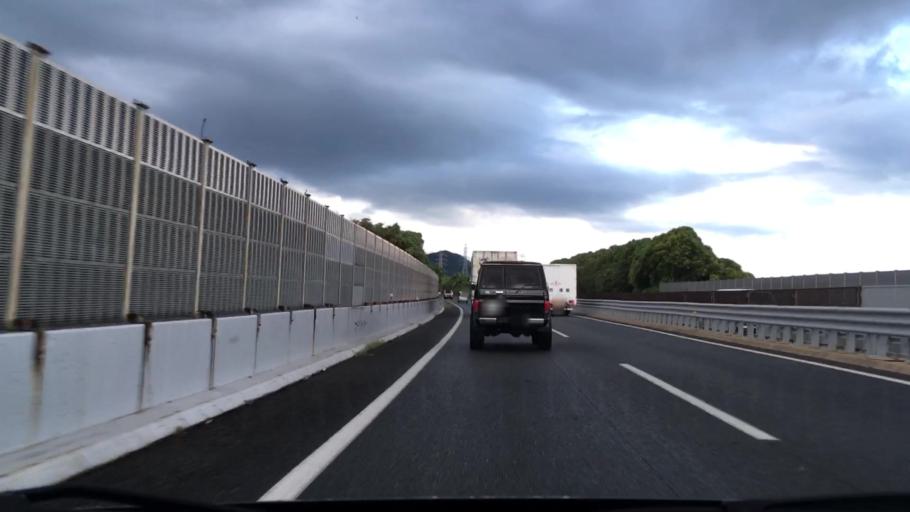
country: JP
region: Fukuoka
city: Kanda
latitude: 33.8404
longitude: 130.9268
